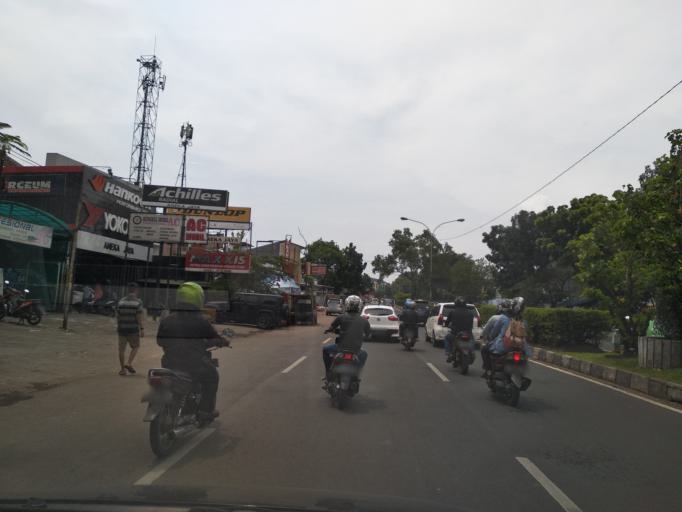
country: ID
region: West Java
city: Bandung
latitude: -6.9375
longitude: 107.5996
